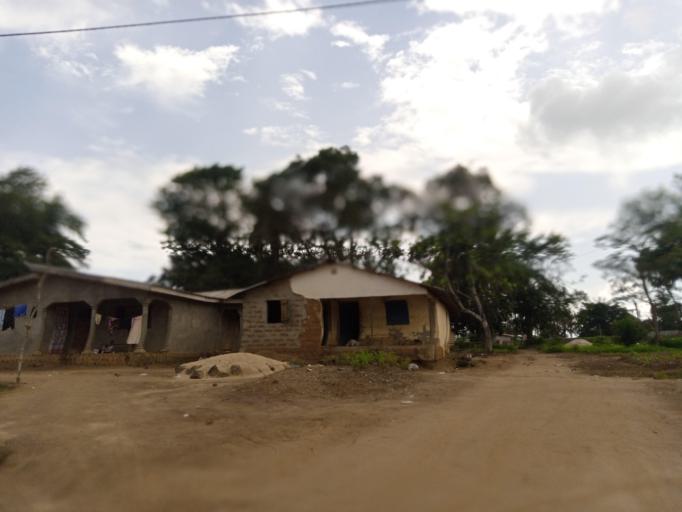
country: SL
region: Northern Province
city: Sawkta
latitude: 8.6319
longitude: -13.2021
